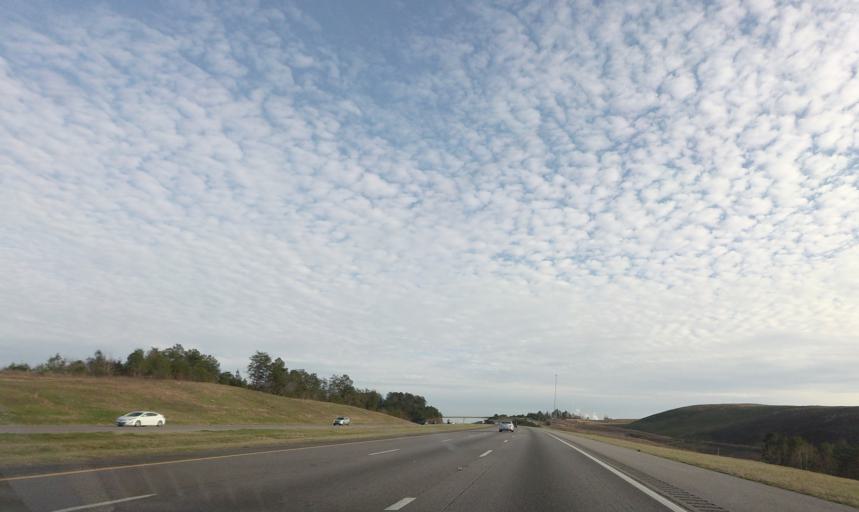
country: US
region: Alabama
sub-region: Walker County
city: Dora
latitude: 33.6968
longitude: -87.1298
